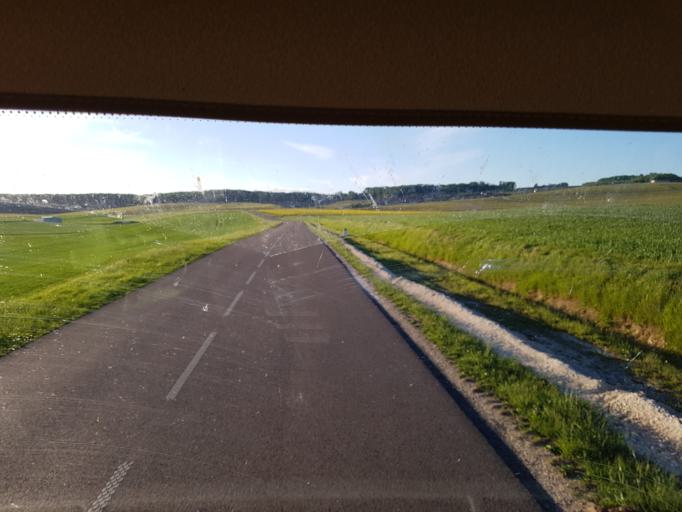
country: FR
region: Champagne-Ardenne
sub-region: Departement de l'Aube
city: Villenauxe-la-Grande
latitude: 48.5988
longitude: 3.6231
